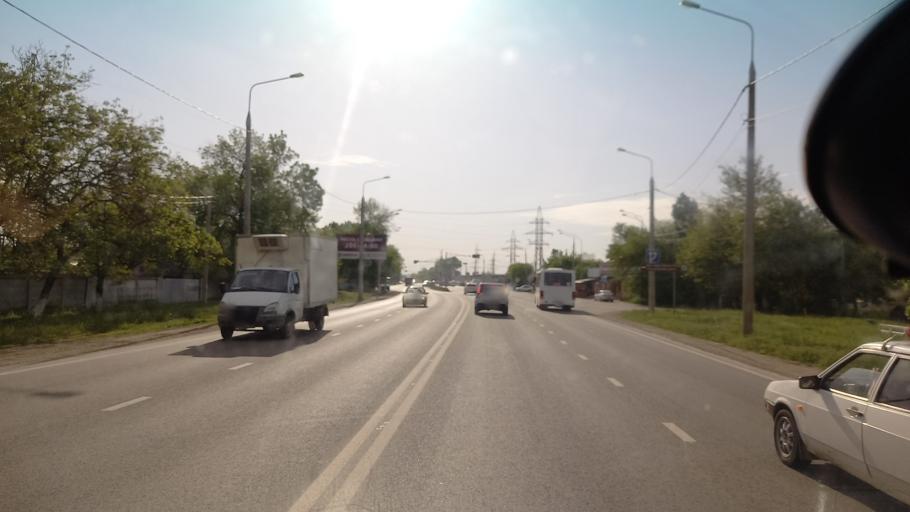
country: RU
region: Krasnodarskiy
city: Krasnodar
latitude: 45.0563
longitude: 38.8985
